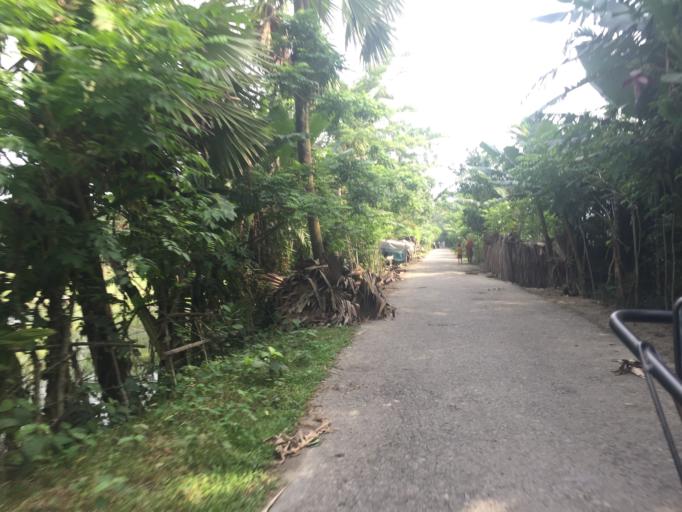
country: BD
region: Barisal
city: Mathba
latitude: 22.2377
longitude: 89.9150
